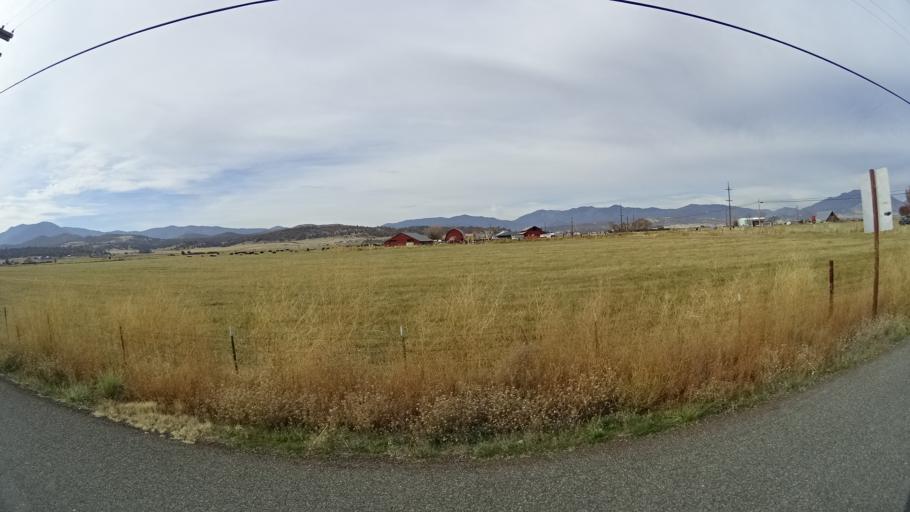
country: US
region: California
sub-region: Siskiyou County
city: Montague
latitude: 41.7050
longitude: -122.5496
